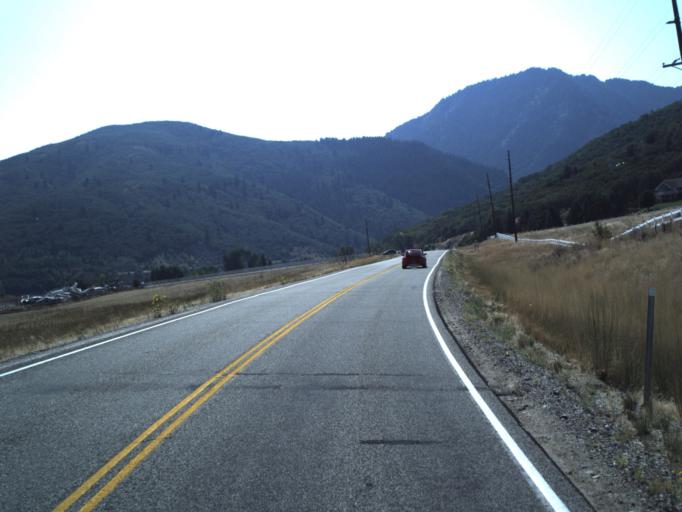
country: US
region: Utah
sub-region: Weber County
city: Wolf Creek
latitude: 41.2710
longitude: -111.8209
